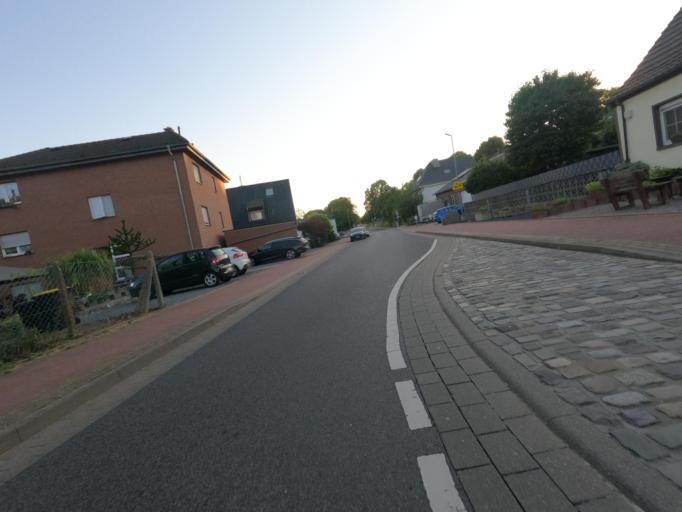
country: DE
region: North Rhine-Westphalia
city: Julich
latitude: 50.9722
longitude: 6.3352
